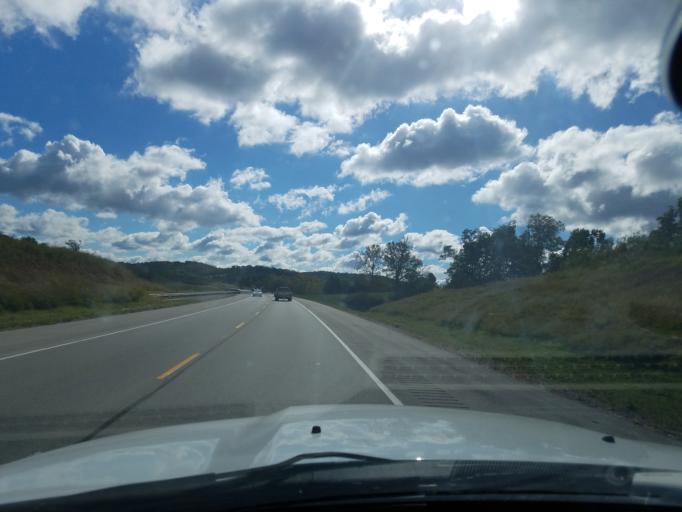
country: US
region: Kentucky
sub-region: Rockcastle County
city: Brodhead
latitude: 37.3571
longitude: -84.4049
